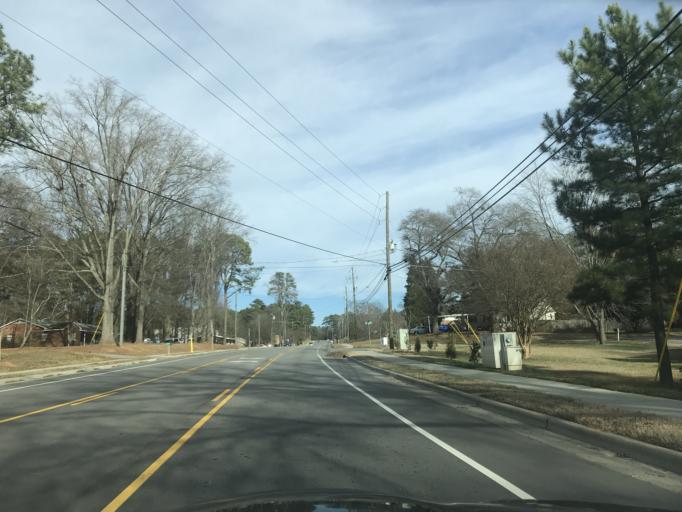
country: US
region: North Carolina
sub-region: Wake County
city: Cary
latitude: 35.7802
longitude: -78.7293
